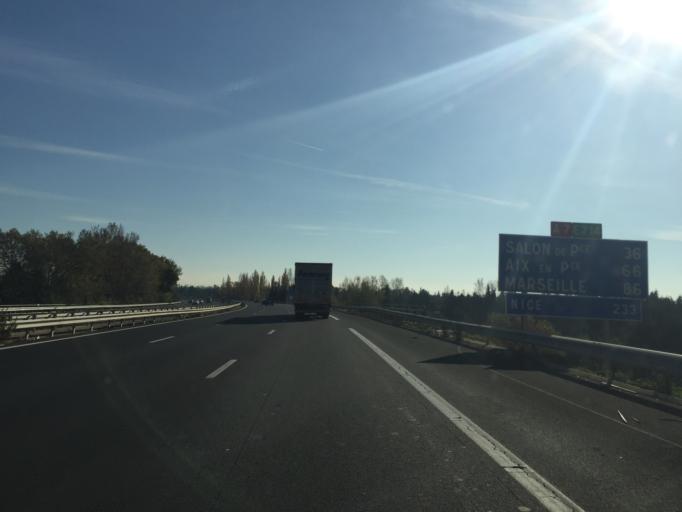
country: FR
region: Provence-Alpes-Cote d'Azur
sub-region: Departement des Bouches-du-Rhone
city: Noves
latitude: 43.8831
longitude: 4.9244
